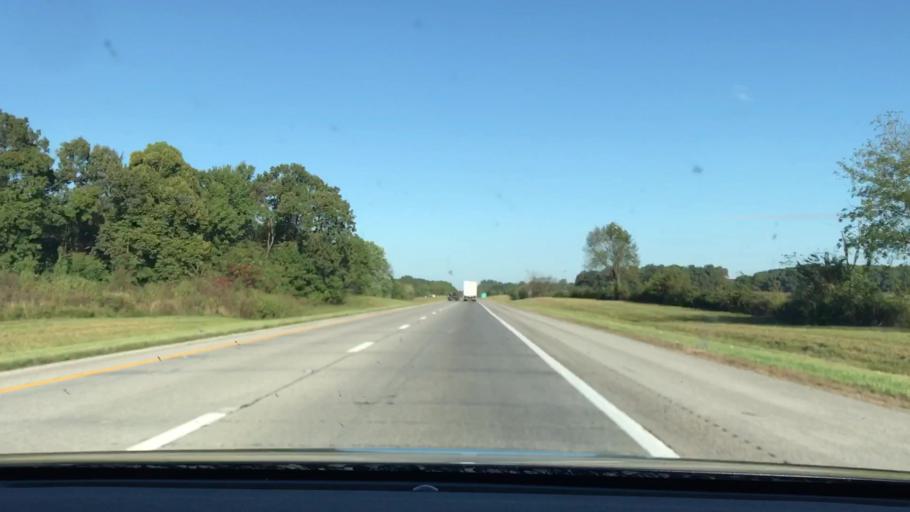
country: US
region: Kentucky
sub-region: Trigg County
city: Cadiz
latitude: 36.9423
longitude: -87.8303
